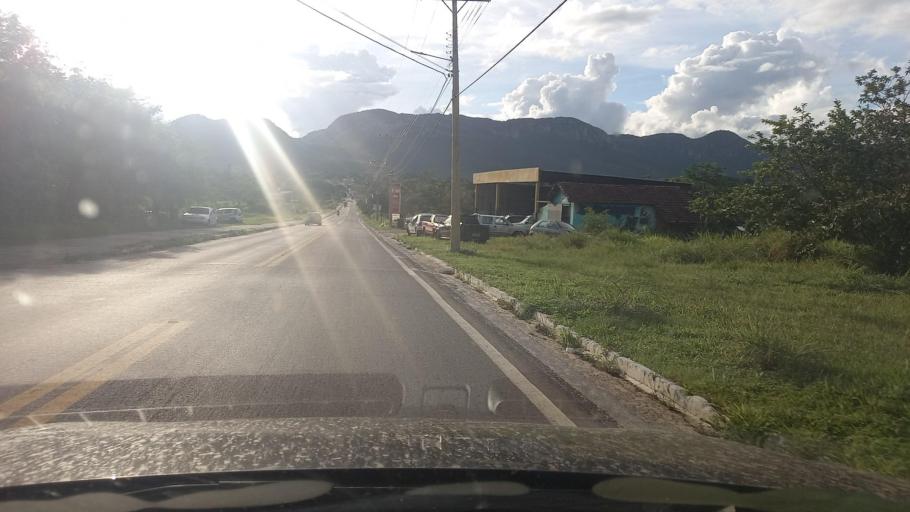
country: BR
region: Goias
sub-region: Cavalcante
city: Cavalcante
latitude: -13.7966
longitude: -47.4513
